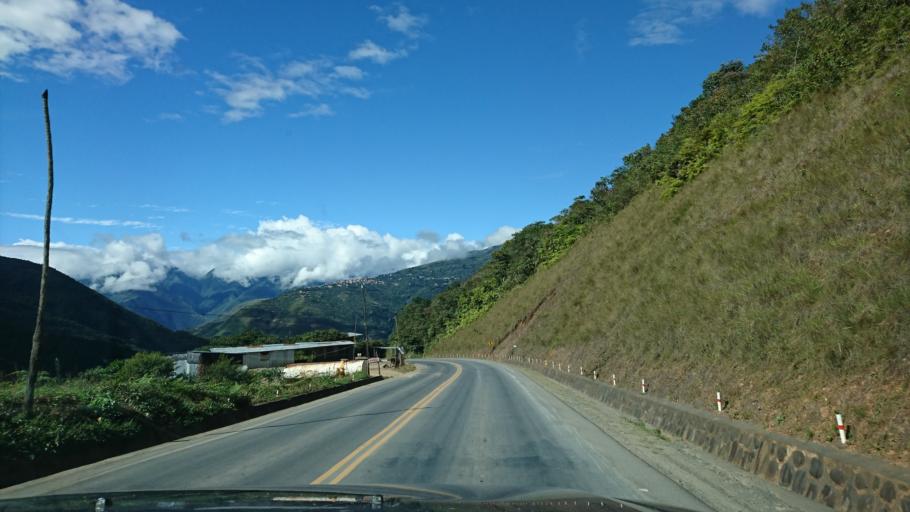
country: BO
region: La Paz
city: Coroico
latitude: -16.2051
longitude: -67.7783
